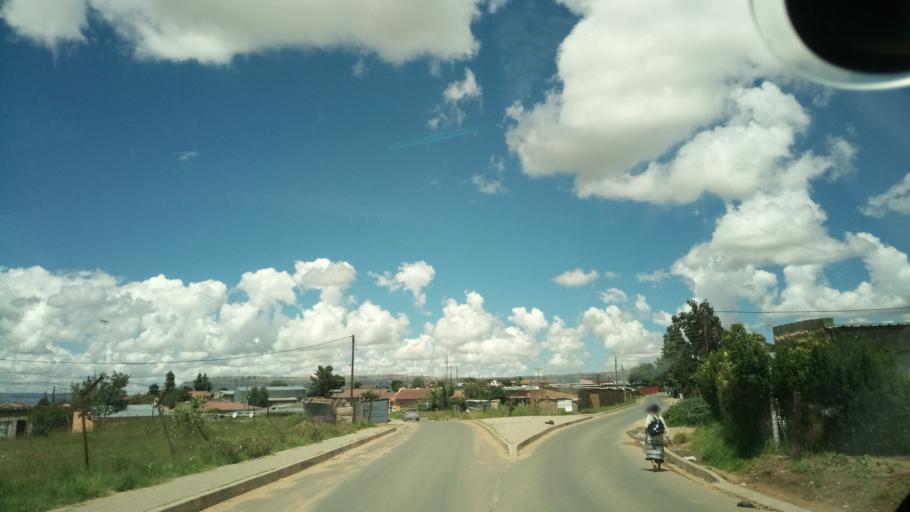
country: LS
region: Maseru
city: Maseru
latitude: -29.3674
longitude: 27.5402
